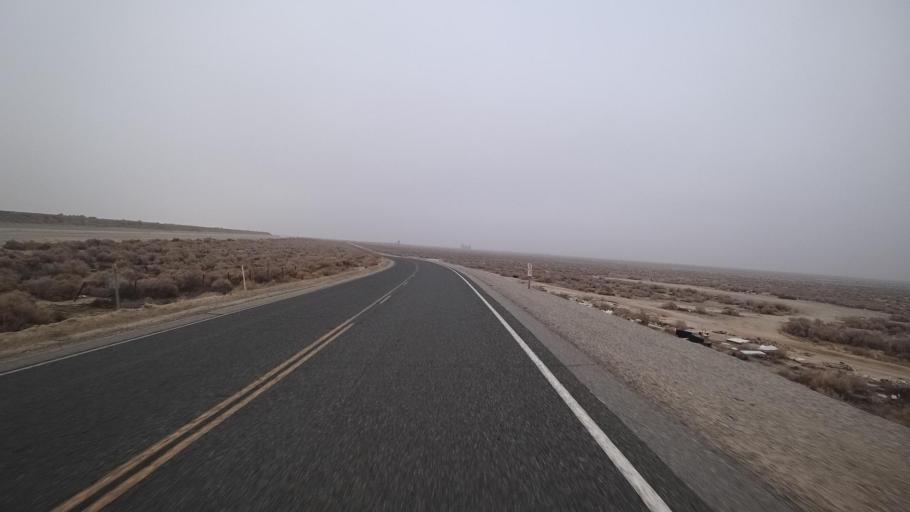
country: US
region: California
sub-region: Kern County
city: Buttonwillow
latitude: 35.3482
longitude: -119.4694
